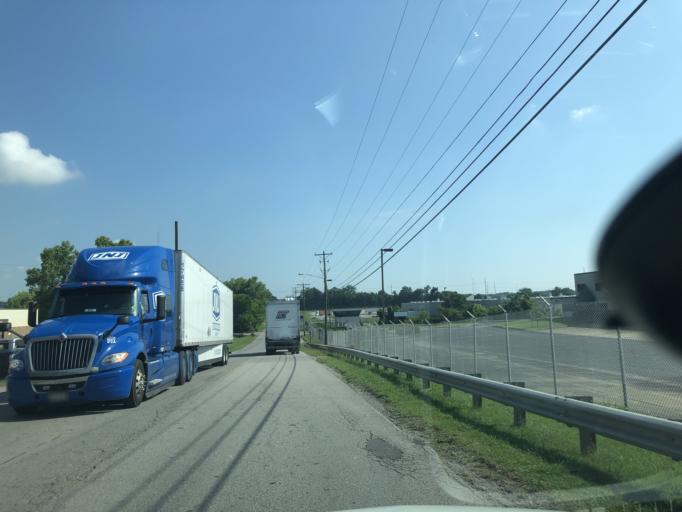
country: US
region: Tennessee
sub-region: Rutherford County
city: La Vergne
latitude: 36.0202
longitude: -86.6067
